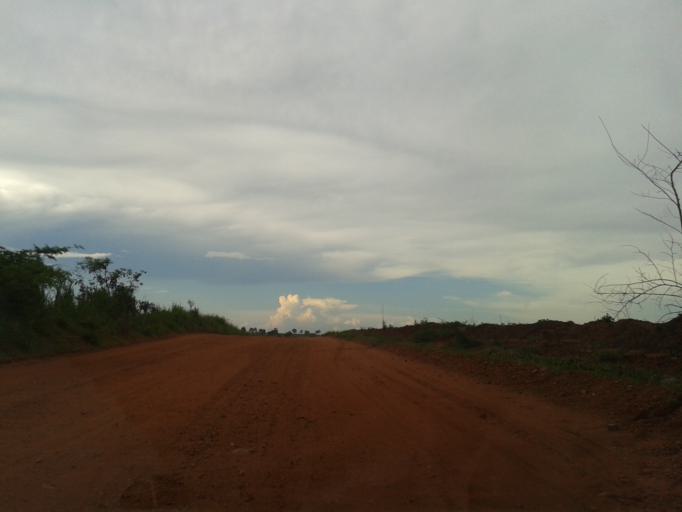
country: BR
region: Minas Gerais
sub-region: Santa Vitoria
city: Santa Vitoria
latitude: -19.0647
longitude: -50.4801
